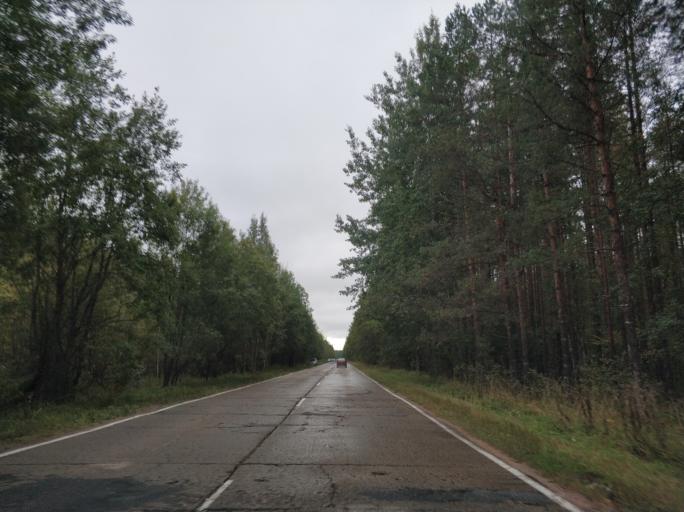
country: RU
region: Leningrad
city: Borisova Griva
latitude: 60.1739
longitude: 30.9194
